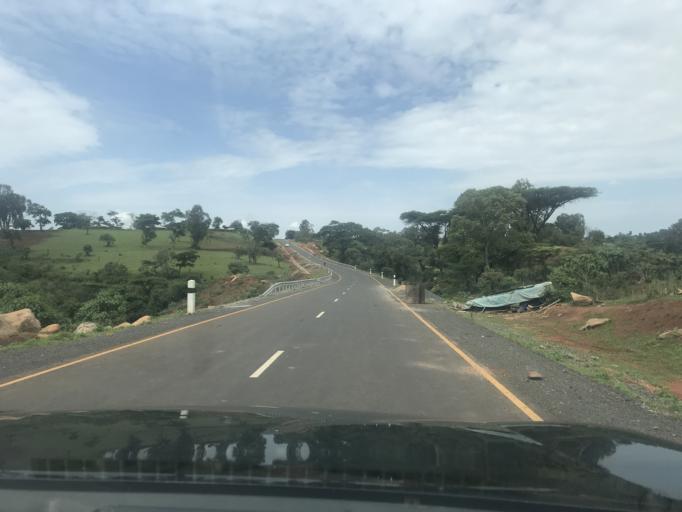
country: ET
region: Oromiya
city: Shambu
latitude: 9.8793
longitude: 36.7100
